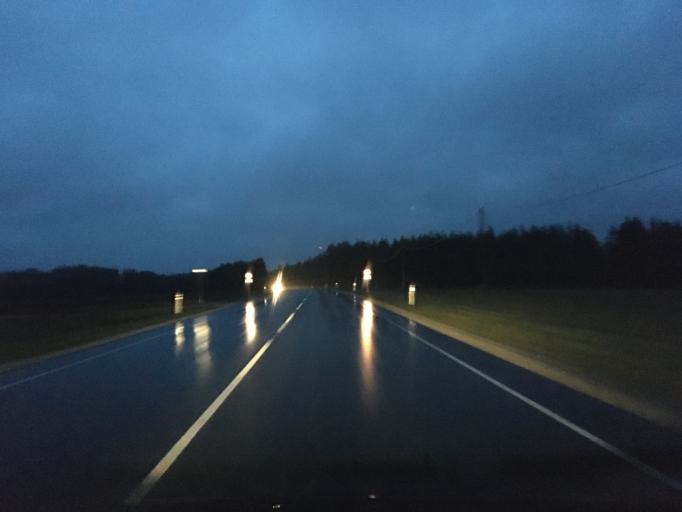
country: EE
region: Harju
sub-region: Nissi vald
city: Turba
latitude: 59.0202
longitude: 24.1446
